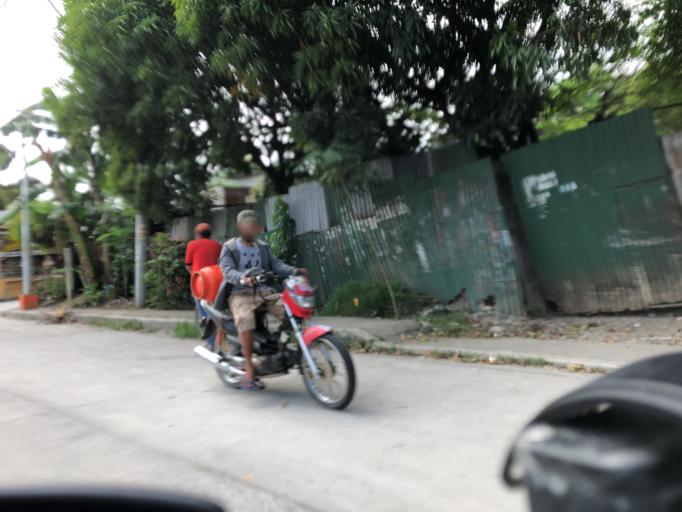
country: PH
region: Central Luzon
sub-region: Province of Bulacan
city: San Jose del Monte
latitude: 14.7498
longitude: 121.0572
